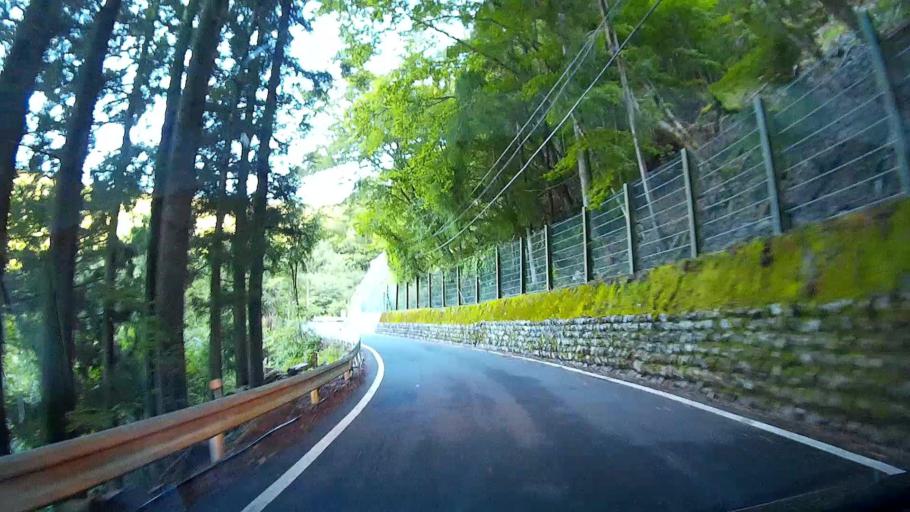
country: JP
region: Shizuoka
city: Shizuoka-shi
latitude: 35.1958
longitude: 138.2368
